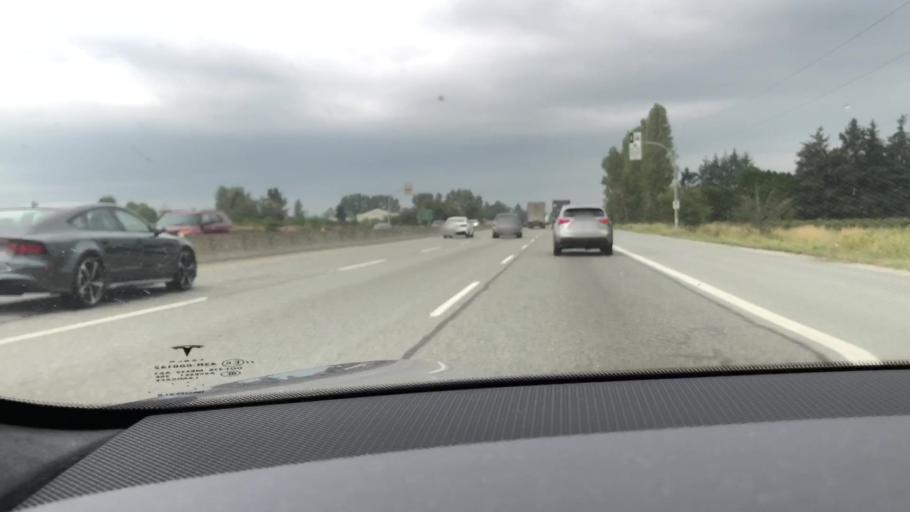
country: CA
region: British Columbia
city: Richmond
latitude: 49.1491
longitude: -123.0864
